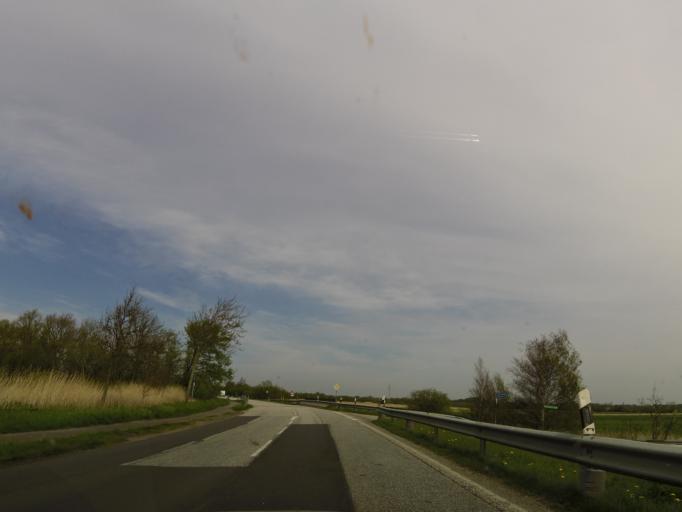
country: DE
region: Schleswig-Holstein
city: Husum
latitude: 54.4480
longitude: 9.0477
